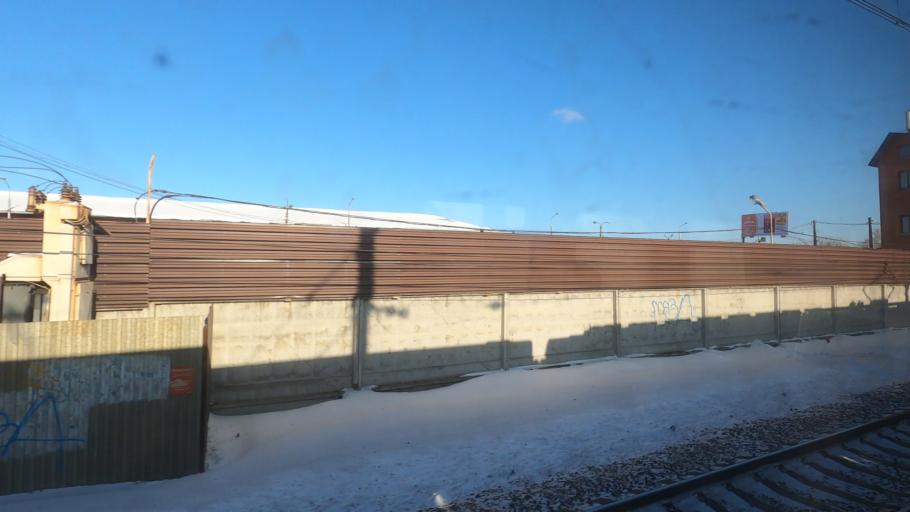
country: RU
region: Moskovskaya
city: Elektrougli
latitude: 55.7325
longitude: 38.1939
